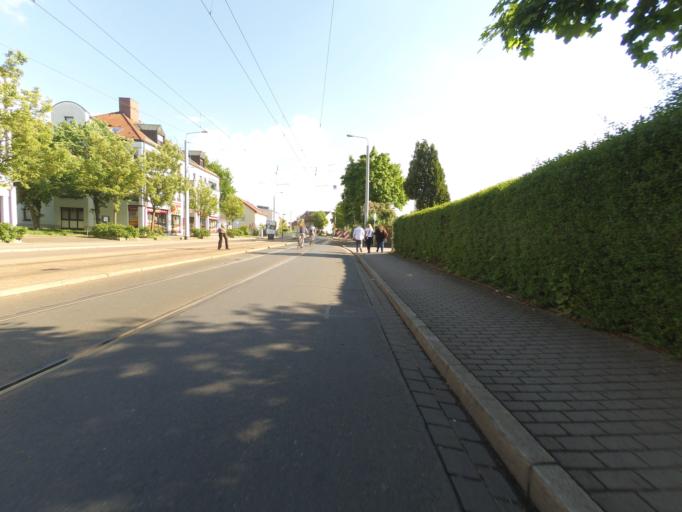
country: DE
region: Saxony
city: Heidenau
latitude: 51.0215
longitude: 13.8116
